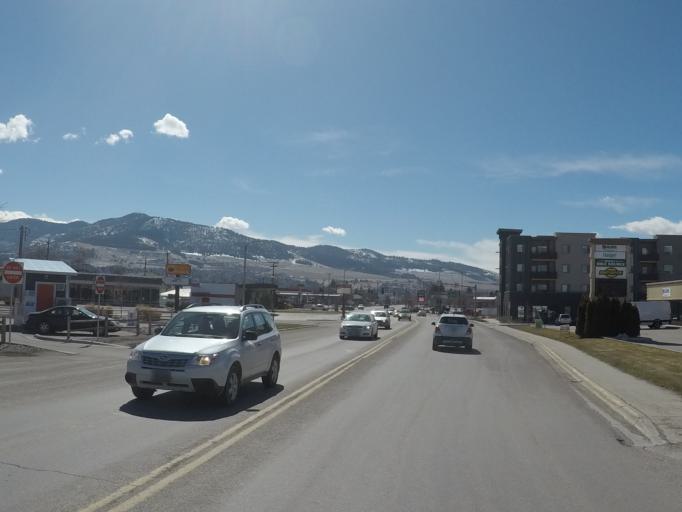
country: US
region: Montana
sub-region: Missoula County
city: Missoula
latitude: 46.8578
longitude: -114.0187
